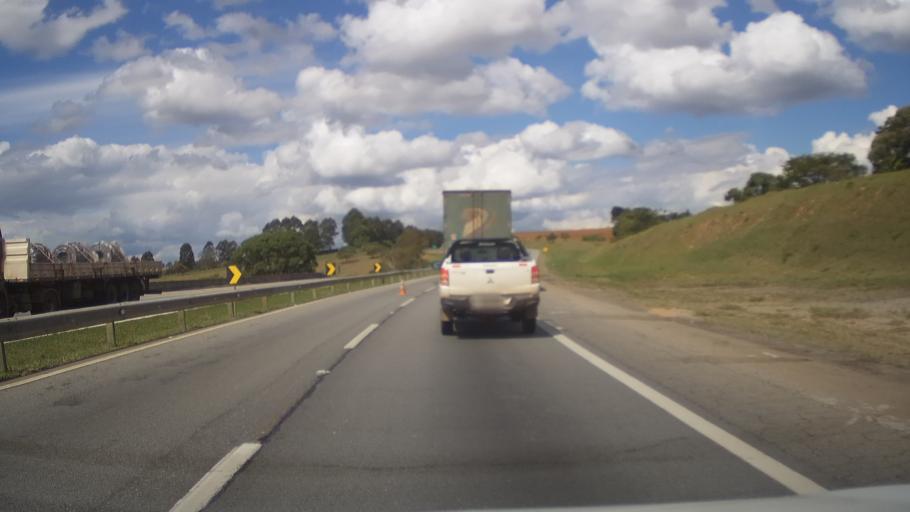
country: BR
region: Minas Gerais
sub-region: Oliveira
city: Oliveira
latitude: -20.8314
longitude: -44.8229
